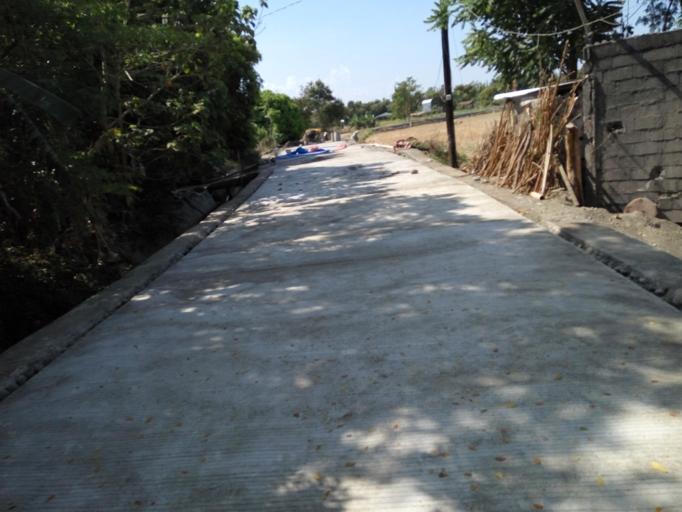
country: PH
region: Ilocos
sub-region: Province of Ilocos Sur
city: Santa Maria
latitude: 16.9462
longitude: 120.4605
